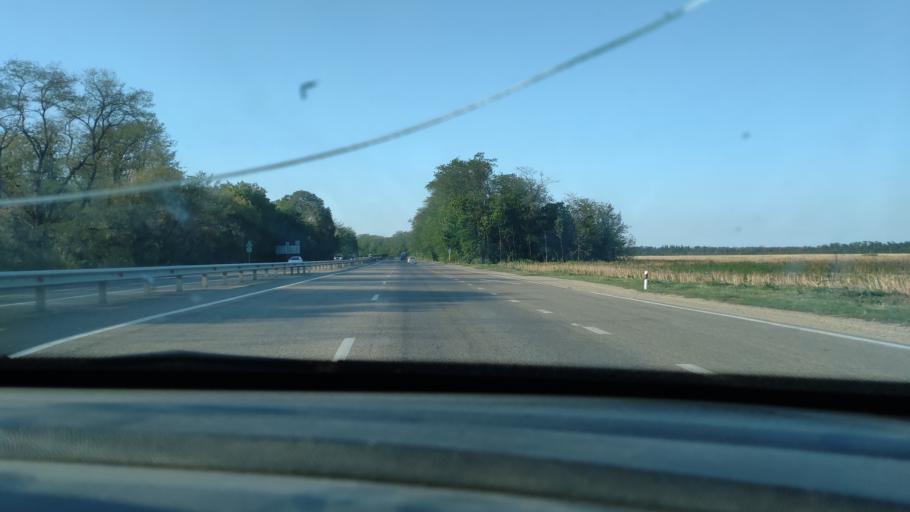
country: RU
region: Krasnodarskiy
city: Timashevsk
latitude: 45.5231
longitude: 38.9420
